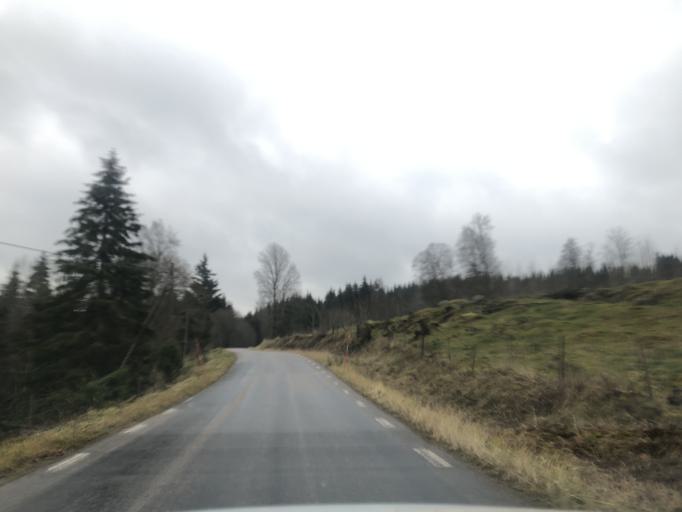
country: SE
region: Vaestra Goetaland
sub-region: Ulricehamns Kommun
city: Ulricehamn
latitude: 57.8800
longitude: 13.5190
